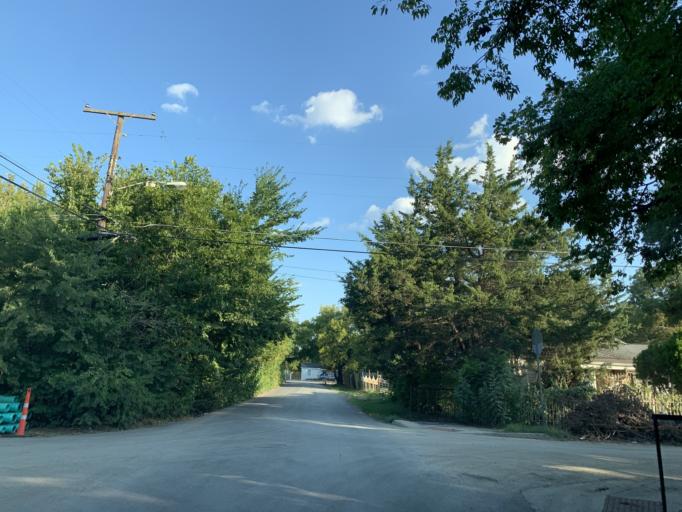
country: US
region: Texas
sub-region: Dallas County
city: Dallas
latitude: 32.6994
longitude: -96.7846
